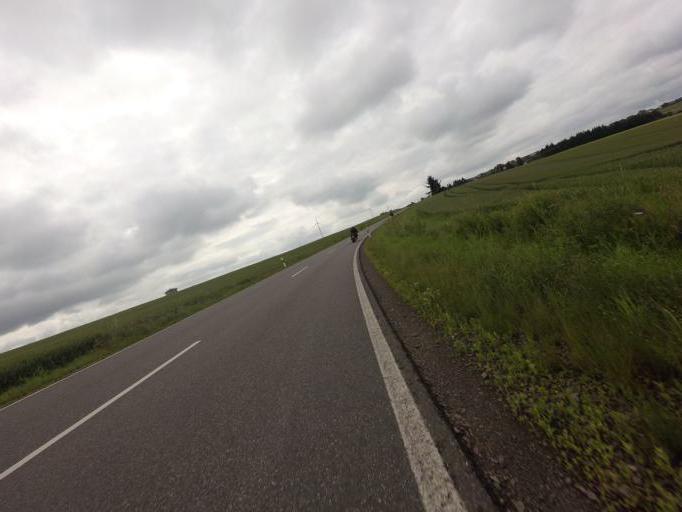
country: DE
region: Rheinland-Pfalz
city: Zilshausen
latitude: 50.1212
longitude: 7.3822
